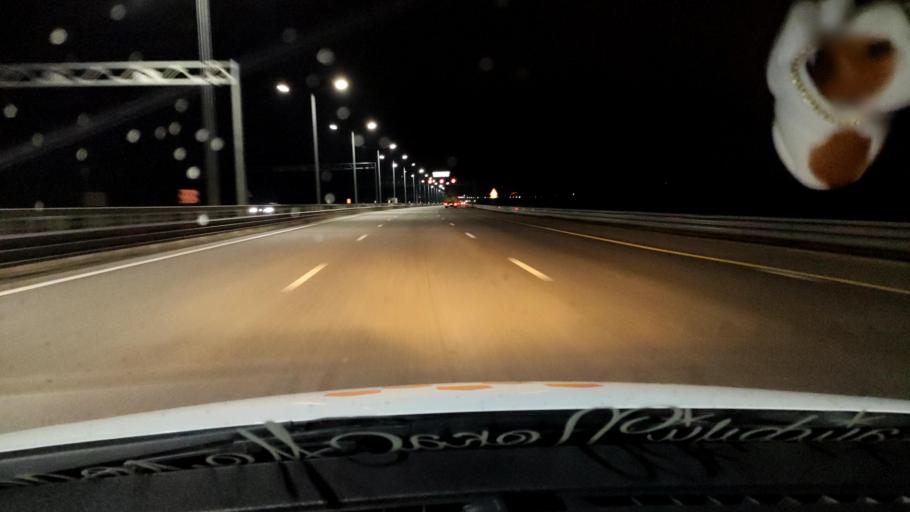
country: RU
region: Voronezj
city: Somovo
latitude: 51.7757
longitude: 39.2995
